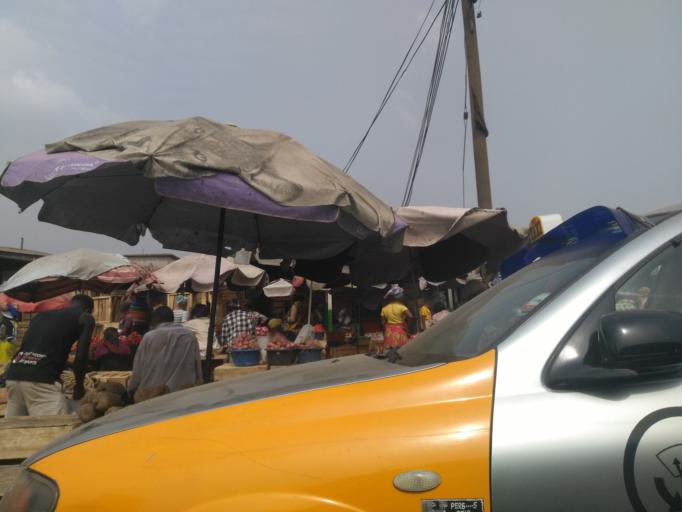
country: GH
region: Greater Accra
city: Accra
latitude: 5.5510
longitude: -0.2213
